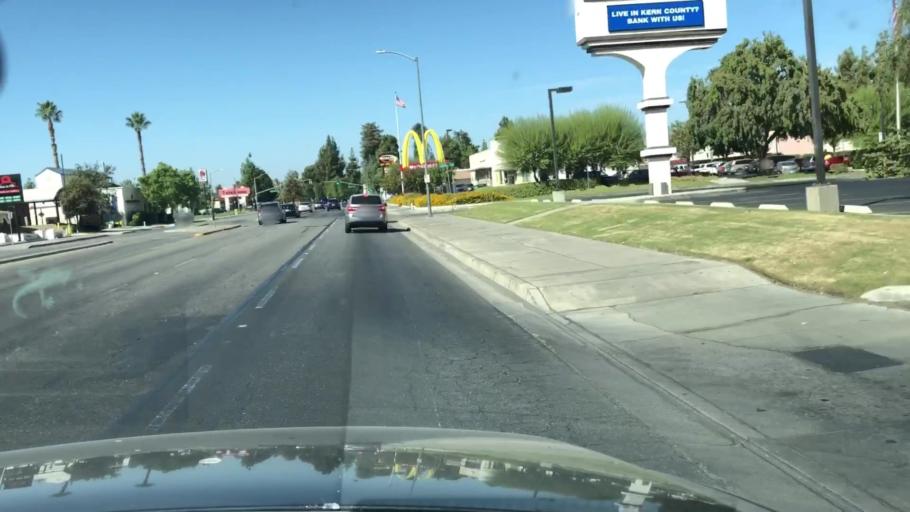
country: US
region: California
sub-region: Kern County
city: Bakersfield
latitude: 35.3397
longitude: -119.0524
